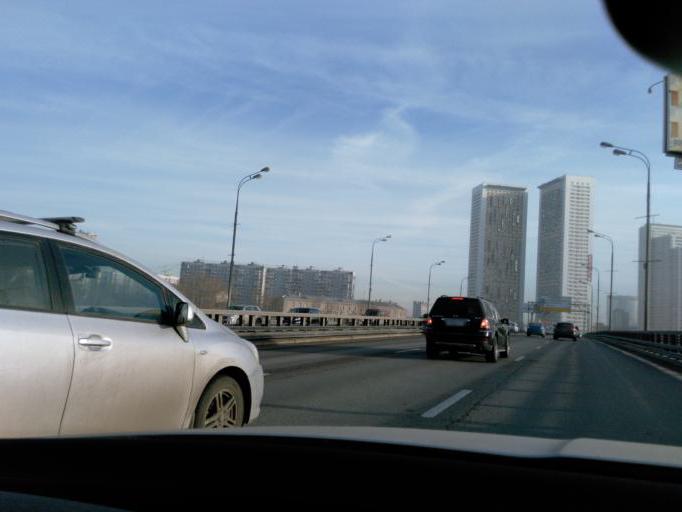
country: RU
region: Moskovskaya
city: Presnenskiy
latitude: 55.7704
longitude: 37.5426
